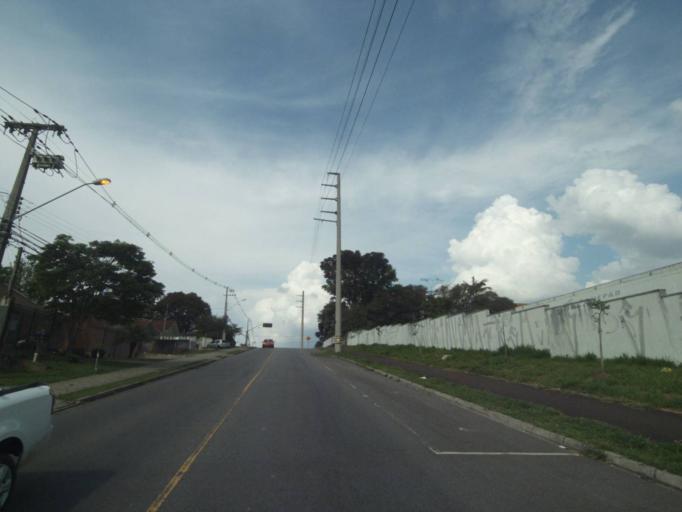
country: BR
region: Parana
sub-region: Pinhais
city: Pinhais
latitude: -25.4081
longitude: -49.2110
